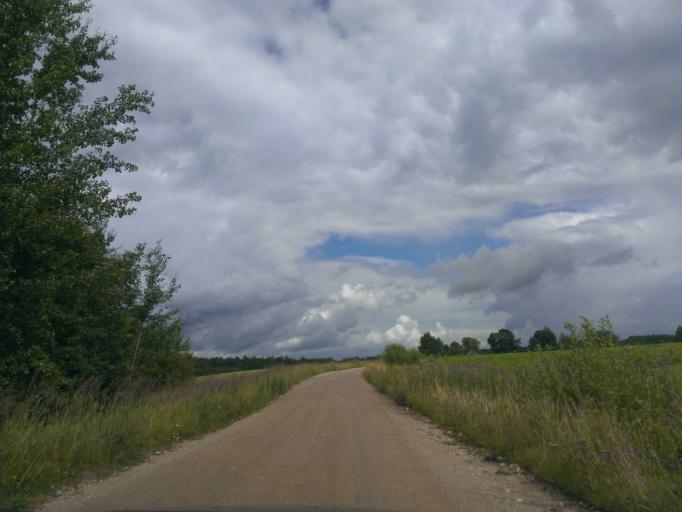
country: LV
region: Ligatne
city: Ligatne
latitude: 57.2030
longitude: 24.9894
